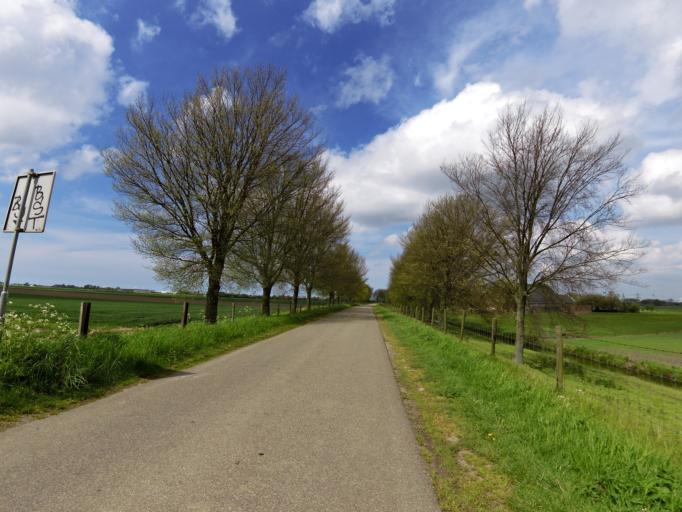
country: NL
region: South Holland
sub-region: Gemeente Hellevoetsluis
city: Nieuwenhoorn
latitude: 51.8443
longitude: 4.2008
